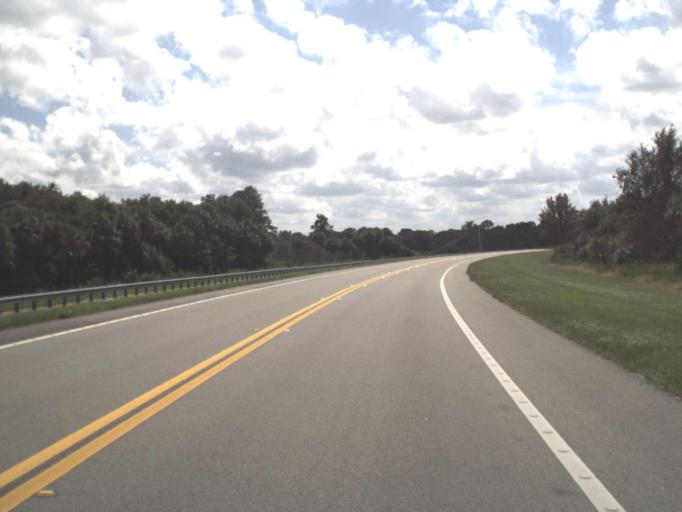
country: US
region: Florida
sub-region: Collier County
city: Immokalee
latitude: 26.3594
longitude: -81.3443
